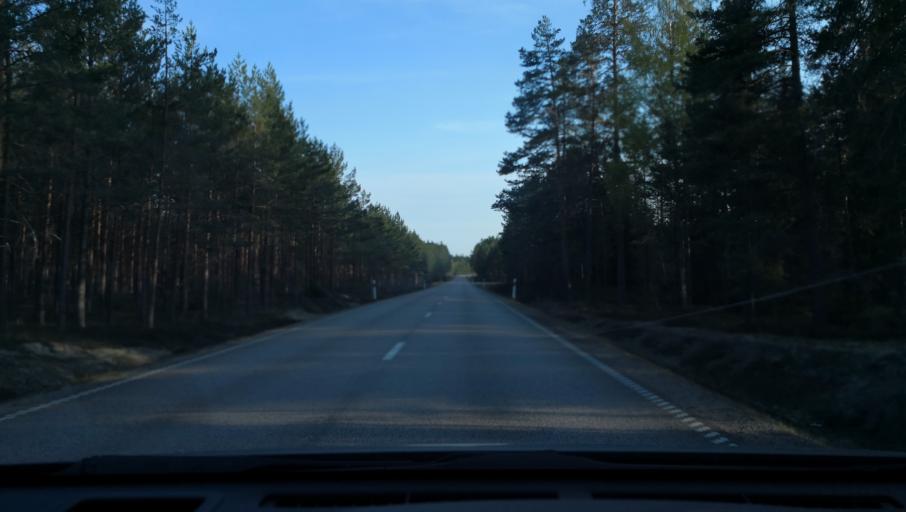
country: SE
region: Uppsala
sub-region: Heby Kommun
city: Heby
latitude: 60.0534
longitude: 16.8659
